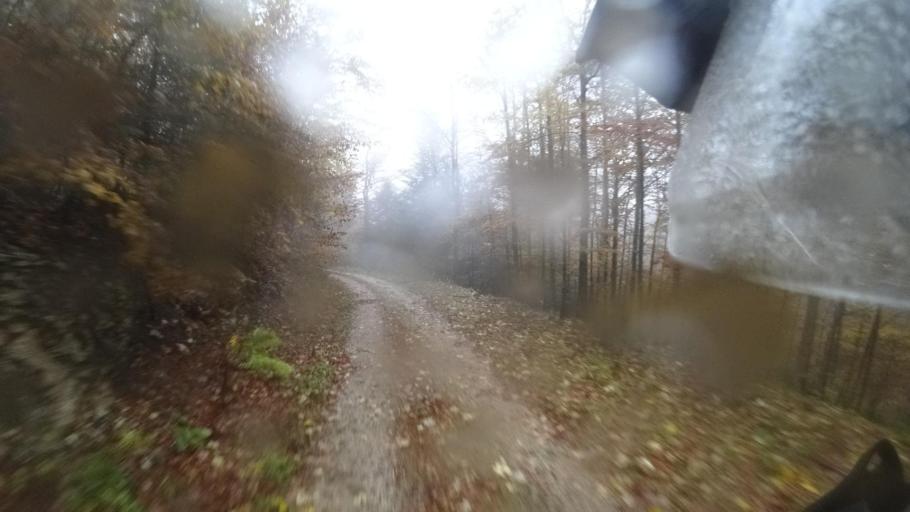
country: HR
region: Primorsko-Goranska
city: Vrbovsko
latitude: 45.2834
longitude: 14.9596
